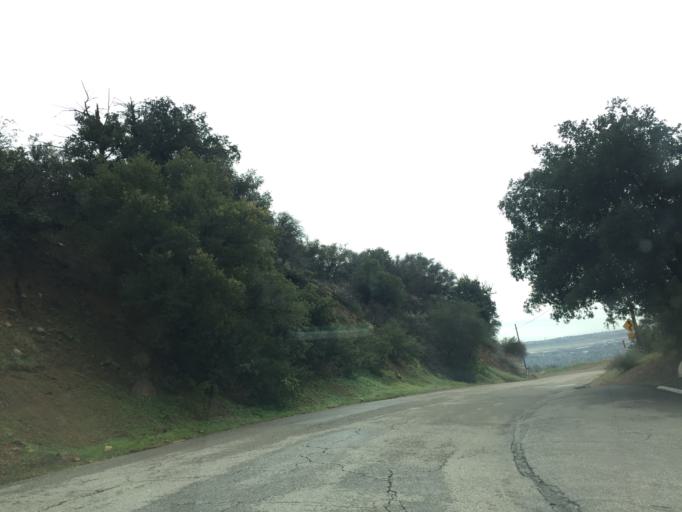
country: US
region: California
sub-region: Santa Barbara County
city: Goleta
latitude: 34.4891
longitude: -119.7959
